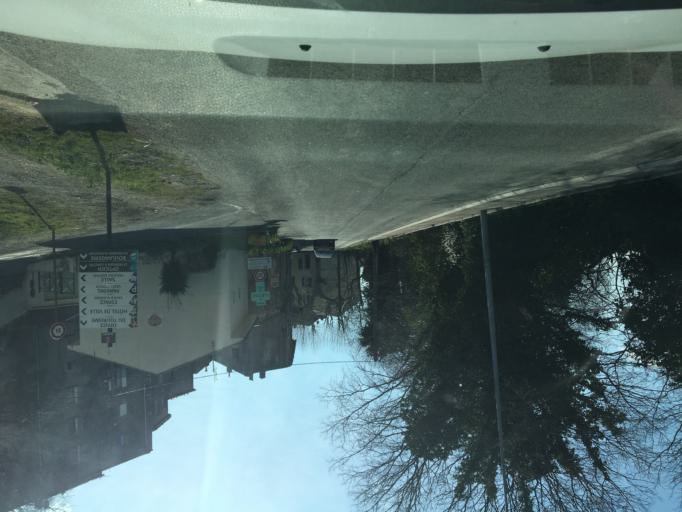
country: FR
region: Provence-Alpes-Cote d'Azur
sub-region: Departement du Var
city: Flayosc
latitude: 43.5342
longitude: 6.3994
